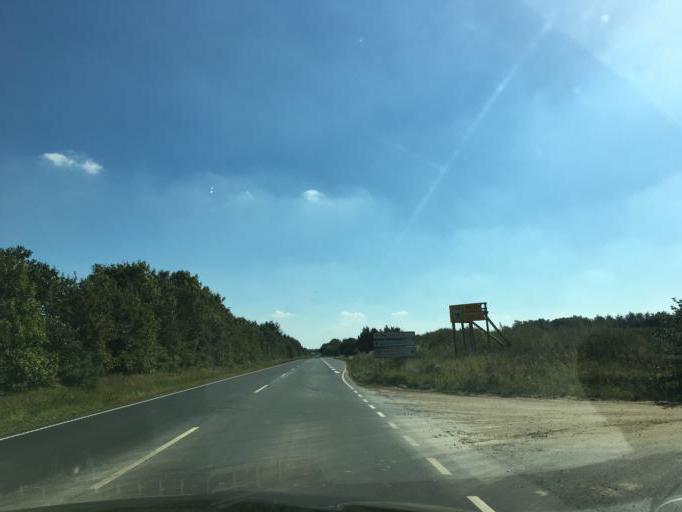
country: DK
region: South Denmark
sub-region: Kolding Kommune
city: Lunderskov
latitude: 55.4980
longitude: 9.2909
